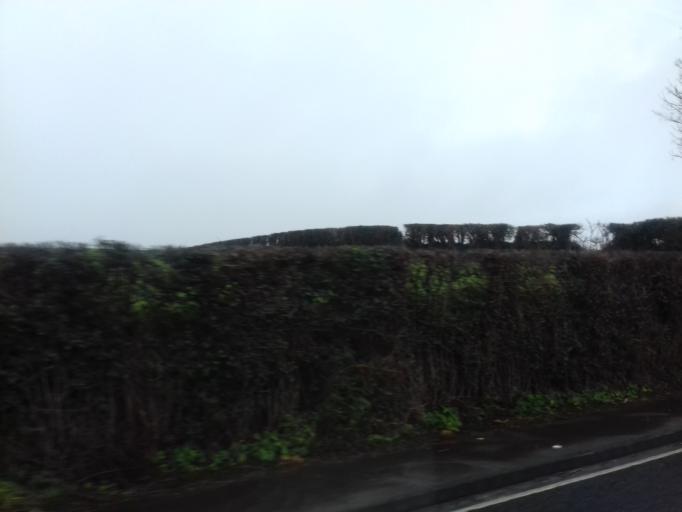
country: GB
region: Northern Ireland
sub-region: Strabane District
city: Sion Mills
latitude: 54.7736
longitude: -7.4659
